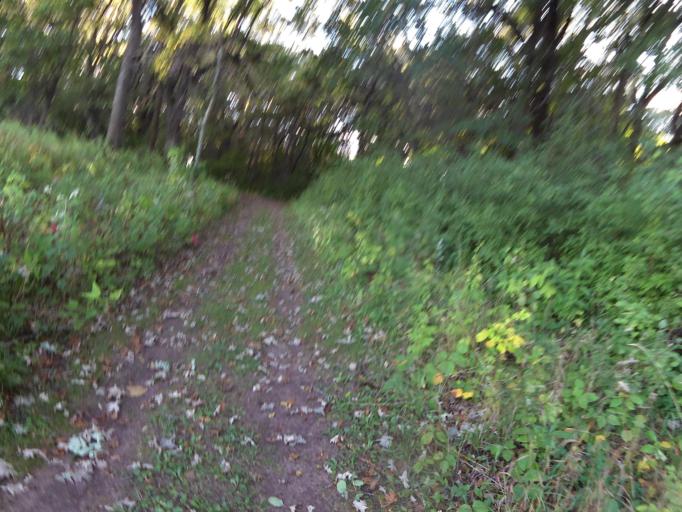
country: US
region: Minnesota
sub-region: Washington County
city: Lake Saint Croix Beach
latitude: 44.9317
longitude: -92.7922
